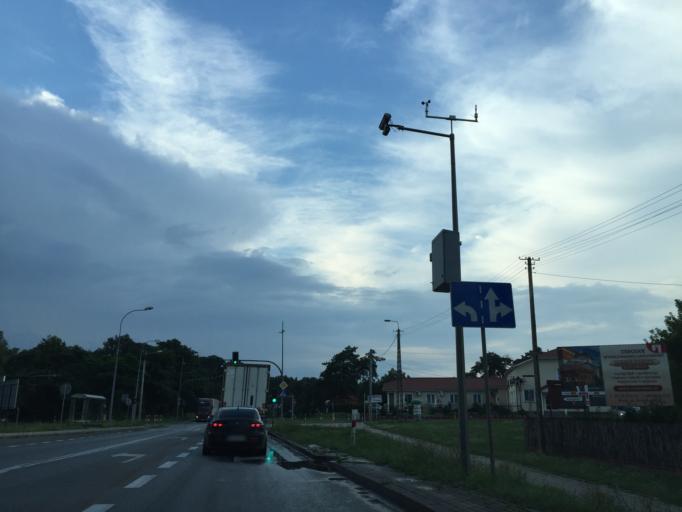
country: PL
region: Masovian Voivodeship
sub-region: Powiat ostrowski
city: Brok
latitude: 52.6967
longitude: 21.8477
